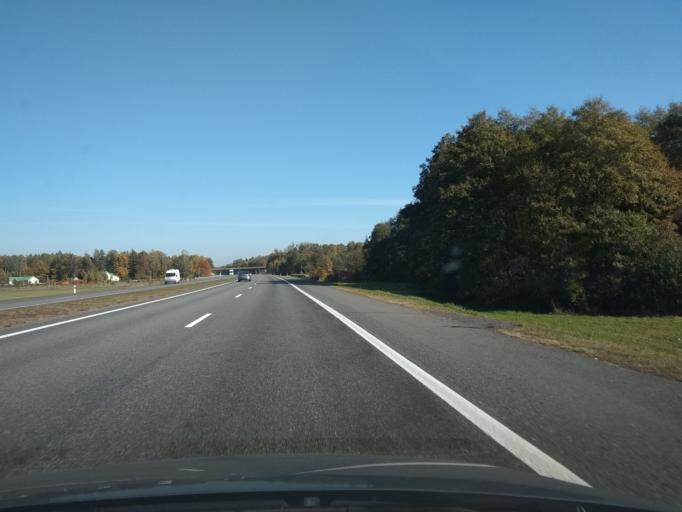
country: BY
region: Brest
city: Ivatsevichy
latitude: 52.6745
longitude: 25.3160
